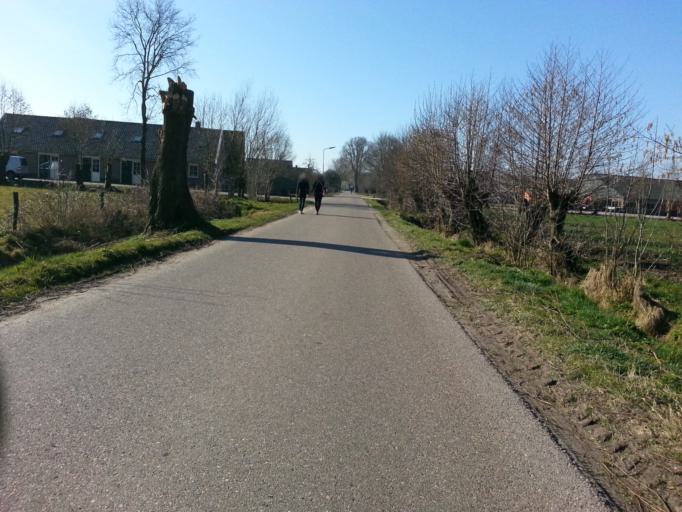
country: NL
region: Utrecht
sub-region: Gemeente Woudenberg
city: Woudenberg
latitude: 52.0775
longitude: 5.4367
